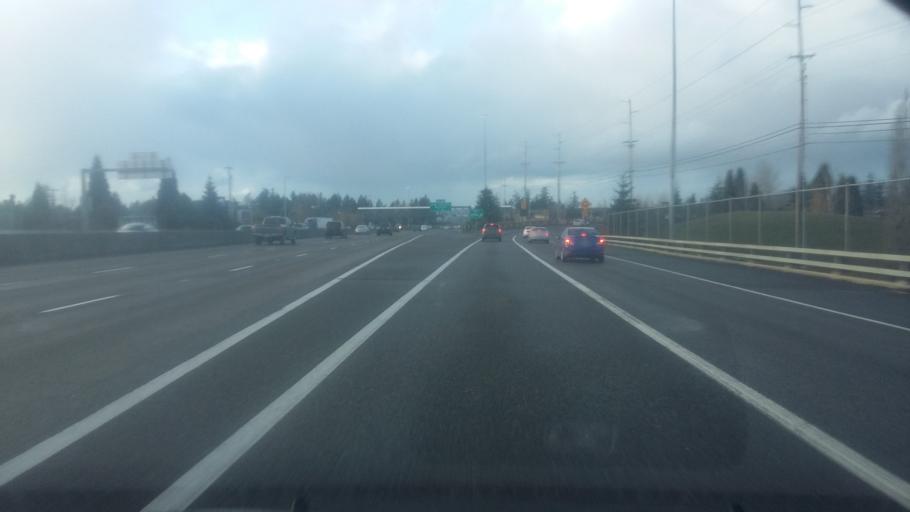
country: US
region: Oregon
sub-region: Washington County
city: West Haven-Sylvan
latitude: 45.5083
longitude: -122.7776
